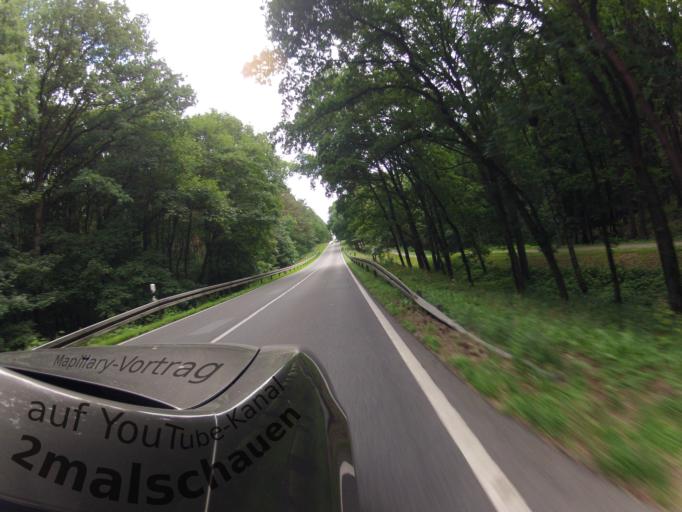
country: DE
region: Mecklenburg-Vorpommern
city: Lassan
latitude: 53.8949
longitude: 13.7875
